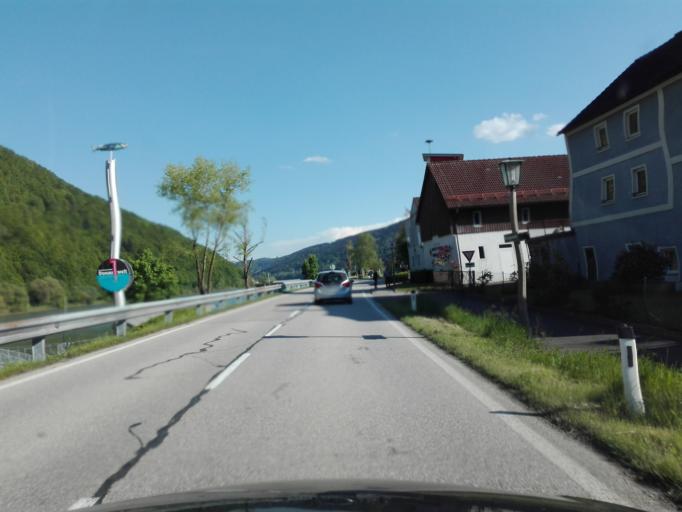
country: AT
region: Upper Austria
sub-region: Politischer Bezirk Rohrbach
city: Pfarrkirchen im Muehlkreis
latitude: 48.5062
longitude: 13.7332
